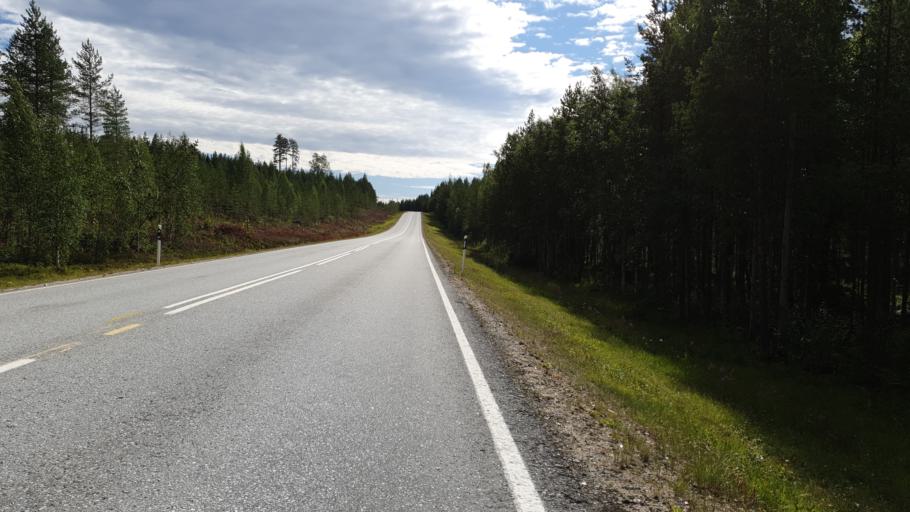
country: FI
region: Kainuu
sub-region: Kehys-Kainuu
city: Kuhmo
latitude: 64.4908
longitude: 29.8467
